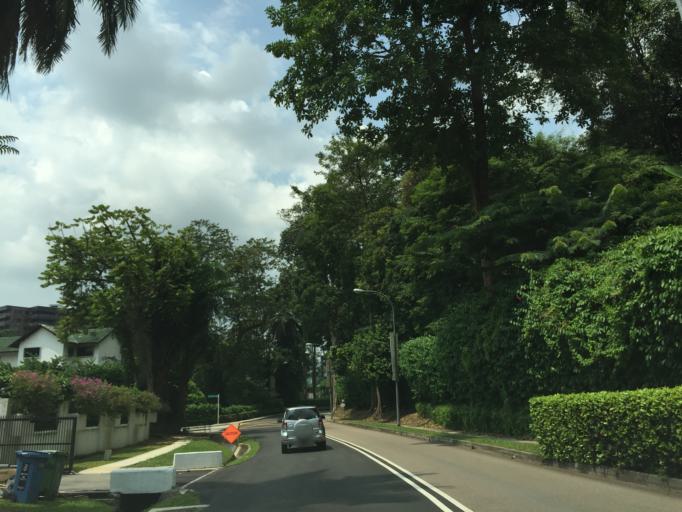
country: SG
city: Singapore
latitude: 1.3117
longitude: 103.8172
